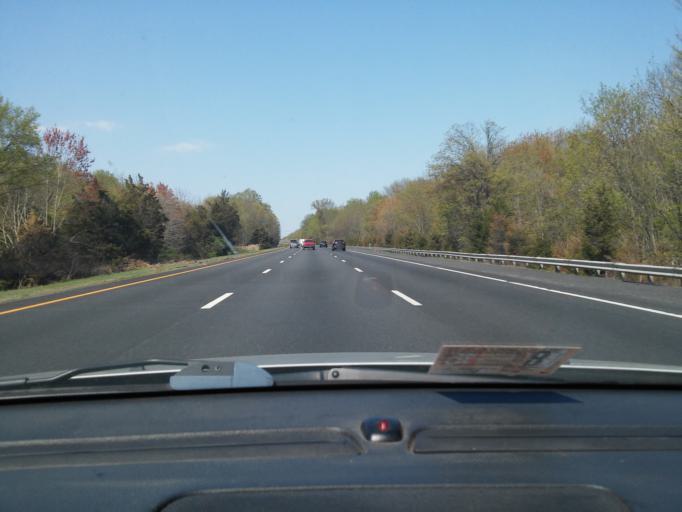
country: US
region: New Jersey
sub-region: Somerset County
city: Watchung
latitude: 40.6492
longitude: -74.4849
